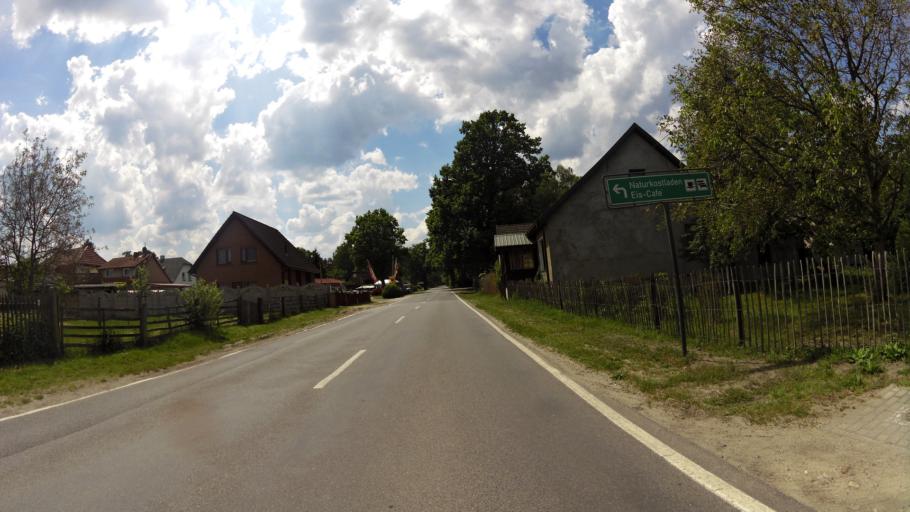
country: DE
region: Brandenburg
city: Gross Koris
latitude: 52.1680
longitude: 13.6857
